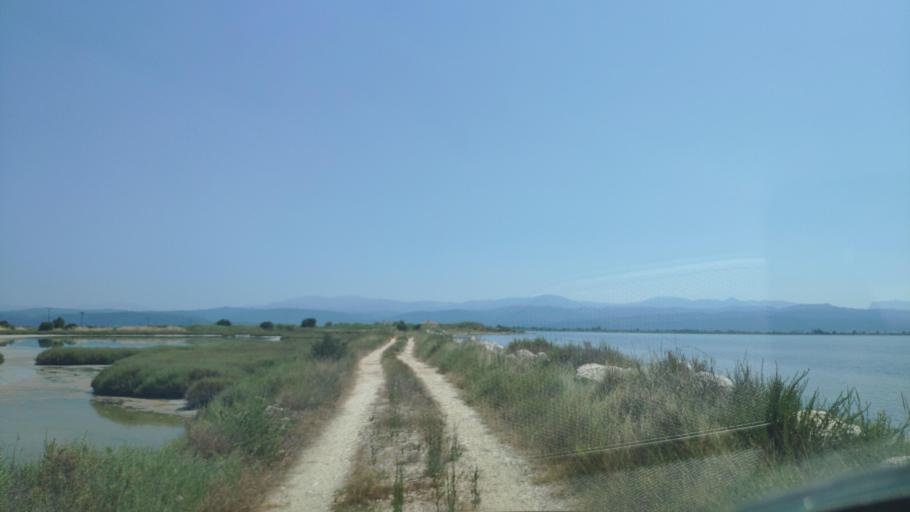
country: GR
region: Epirus
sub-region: Nomos Artas
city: Aneza
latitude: 39.0296
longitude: 20.9459
